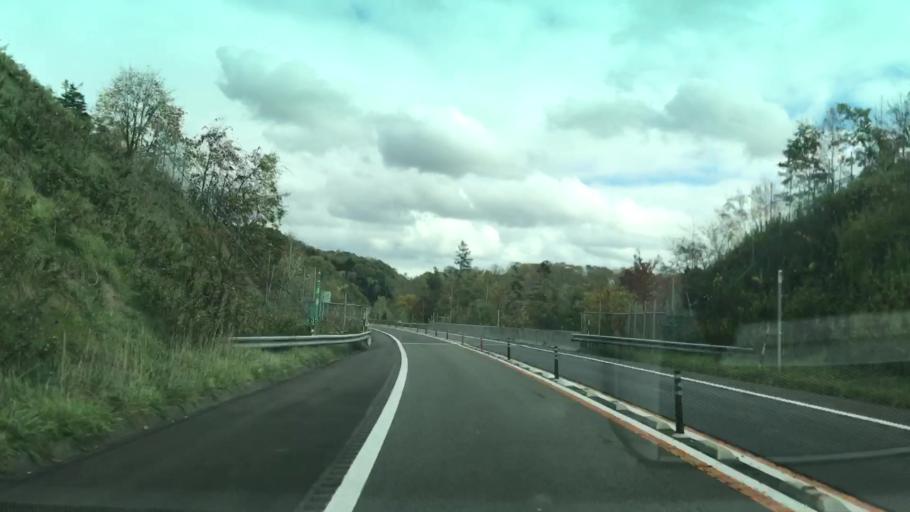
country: JP
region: Hokkaido
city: Chitose
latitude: 42.9160
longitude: 141.9637
